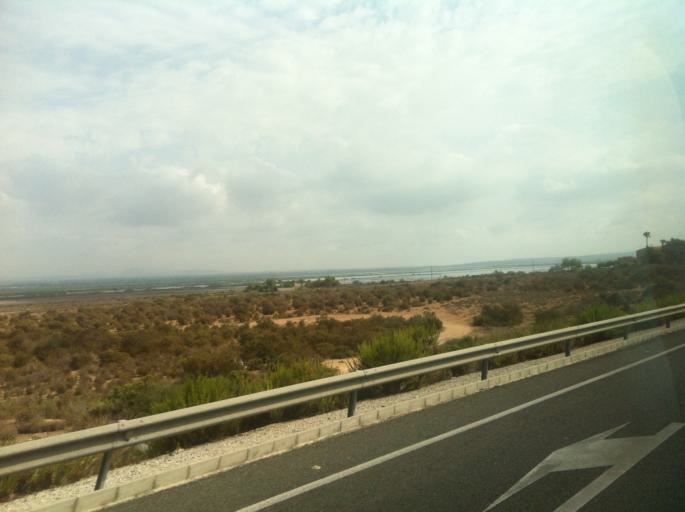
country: ES
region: Valencia
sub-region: Provincia de Alicante
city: Guardamar del Segura
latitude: 38.1599
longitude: -0.6477
